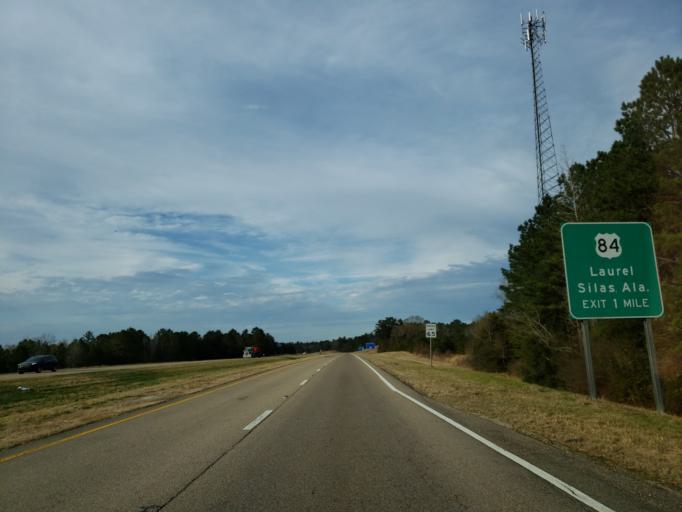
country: US
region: Mississippi
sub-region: Wayne County
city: Waynesboro
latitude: 31.6889
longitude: -88.6173
